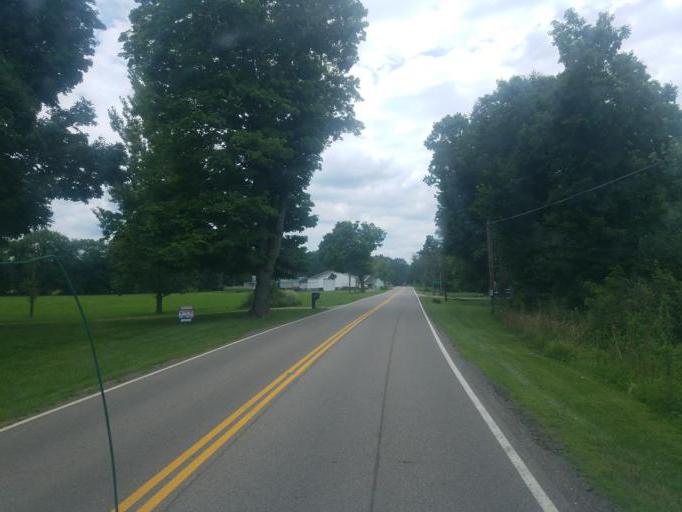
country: US
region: Ohio
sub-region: Licking County
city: Utica
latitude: 40.1597
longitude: -82.4580
